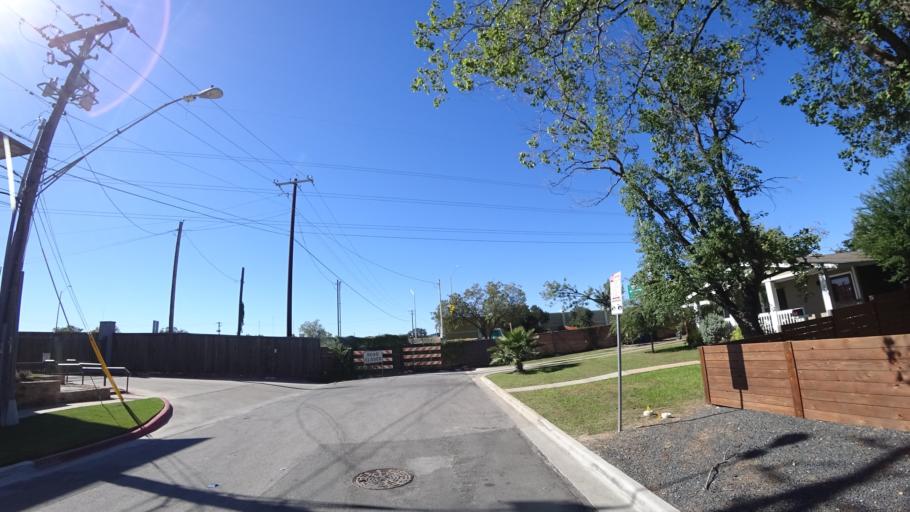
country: US
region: Texas
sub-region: Travis County
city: West Lake Hills
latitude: 30.3202
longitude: -97.7552
